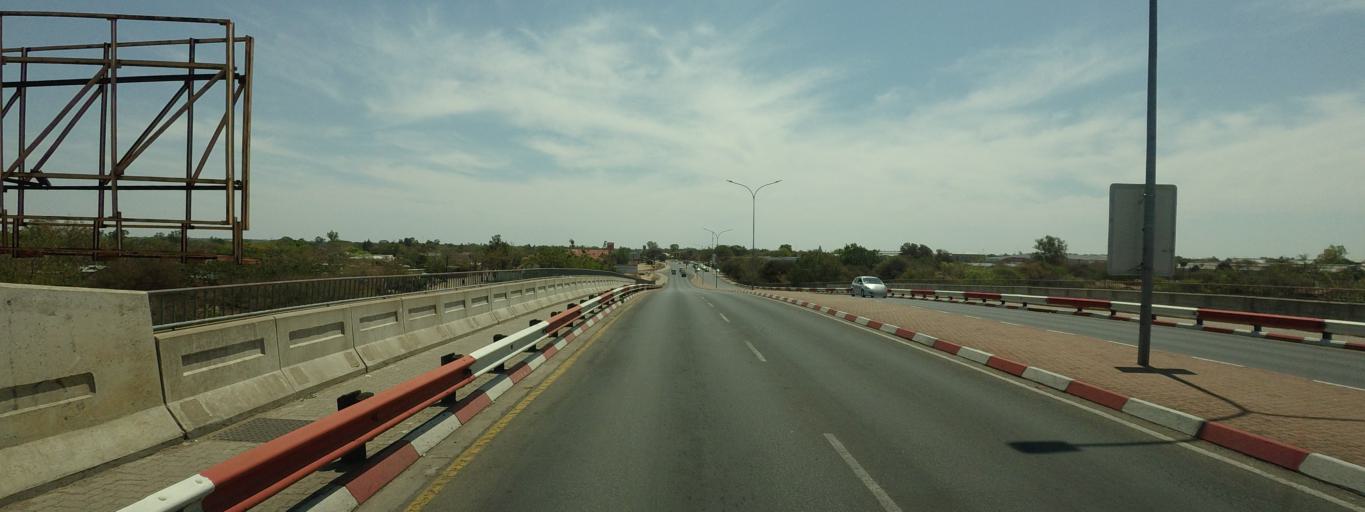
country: BW
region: North East
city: Francistown
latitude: -21.1731
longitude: 27.5098
